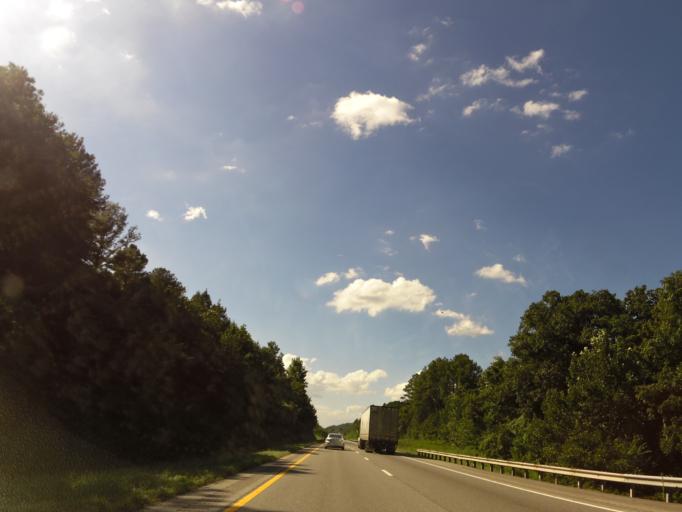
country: US
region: Tennessee
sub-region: Smith County
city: Gordonsville
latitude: 36.1541
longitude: -85.8762
